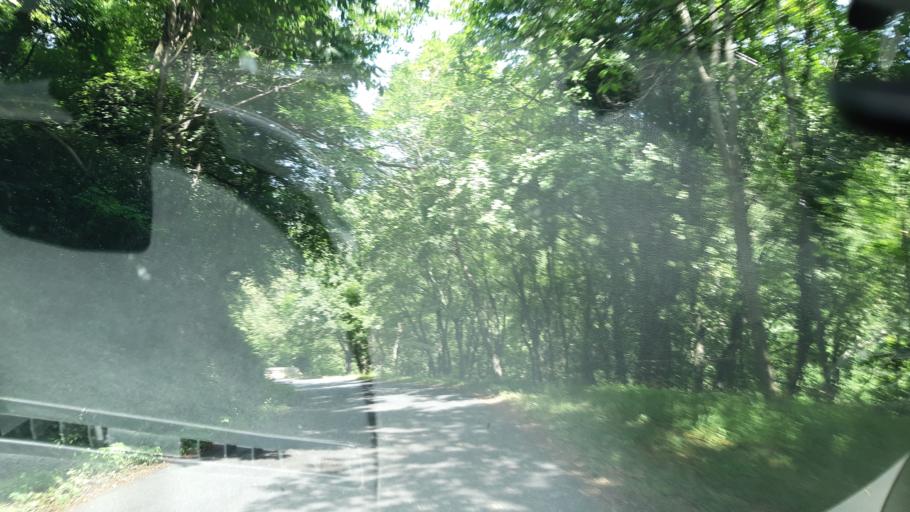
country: FR
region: Languedoc-Roussillon
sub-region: Departement des Pyrenees-Orientales
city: Arles
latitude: 42.5229
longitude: 2.6134
